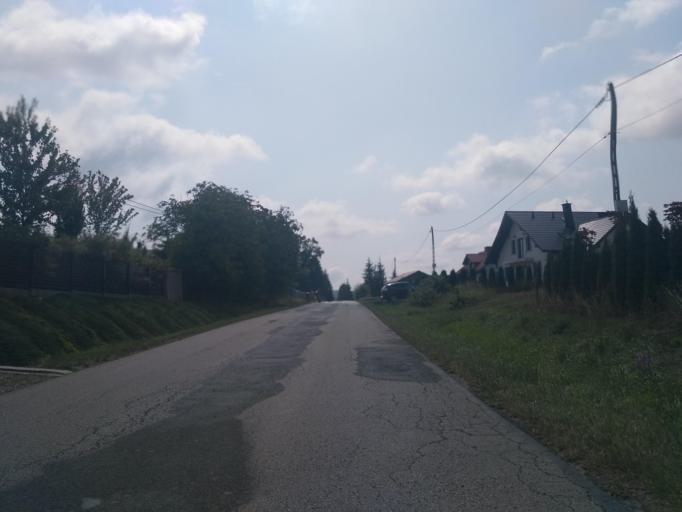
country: PL
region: Subcarpathian Voivodeship
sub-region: Powiat lancucki
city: Kraczkowa
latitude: 50.0318
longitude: 22.1907
